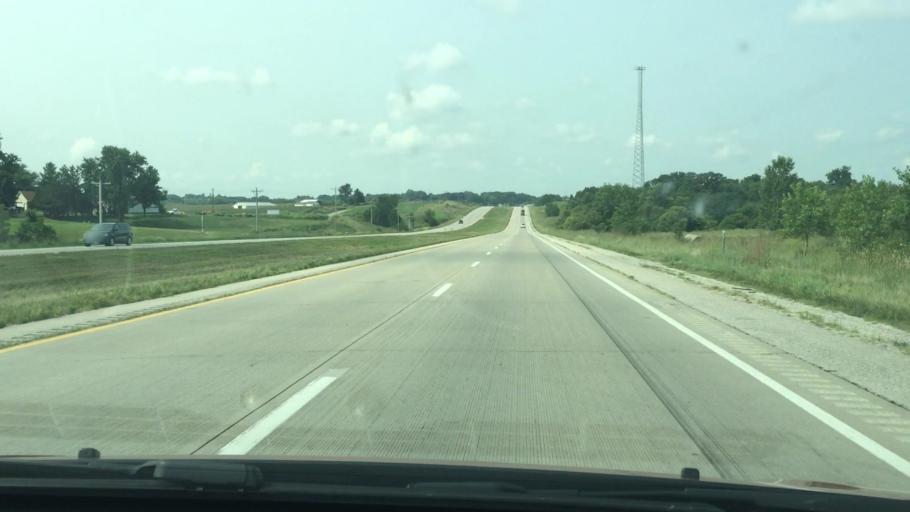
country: US
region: Iowa
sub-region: Cedar County
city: Durant
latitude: 41.5101
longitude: -90.9207
